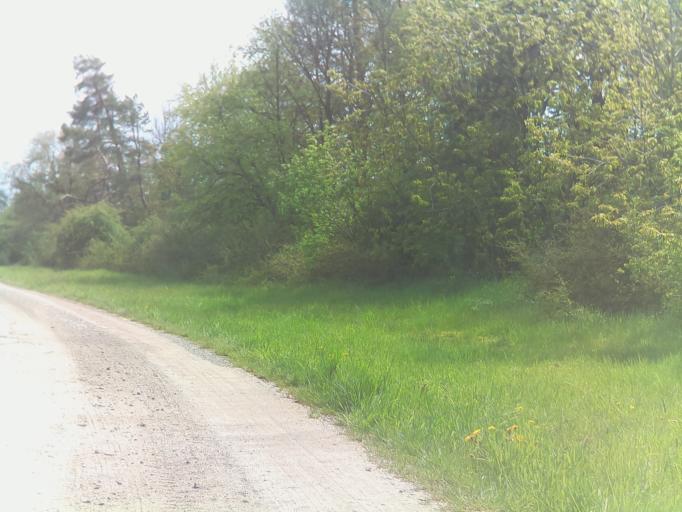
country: DE
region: Thuringia
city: Beinerstadt
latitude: 50.4661
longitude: 10.5513
